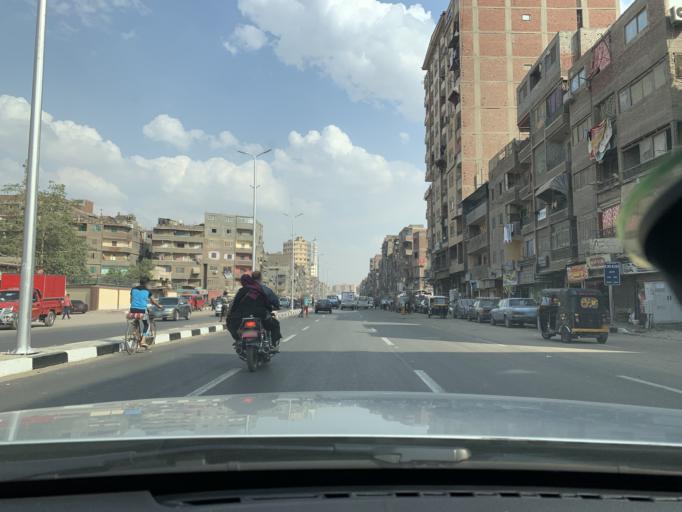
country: EG
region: Muhafazat al Qahirah
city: Cairo
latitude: 30.1235
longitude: 31.3000
